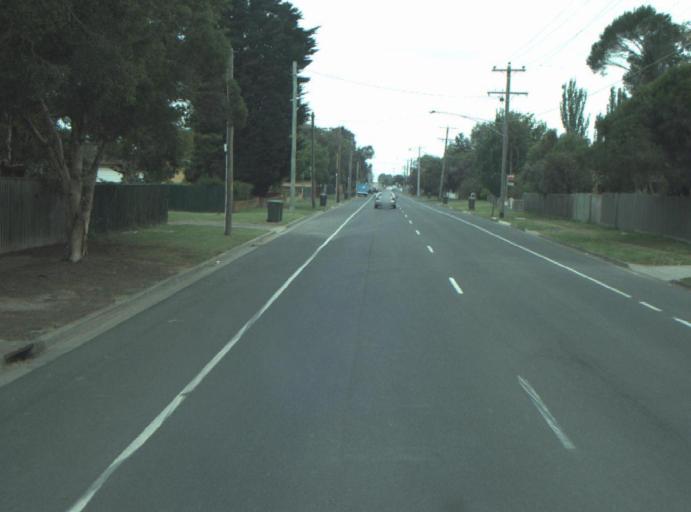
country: AU
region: Victoria
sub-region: Greater Geelong
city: East Geelong
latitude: -38.1699
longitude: 144.4032
